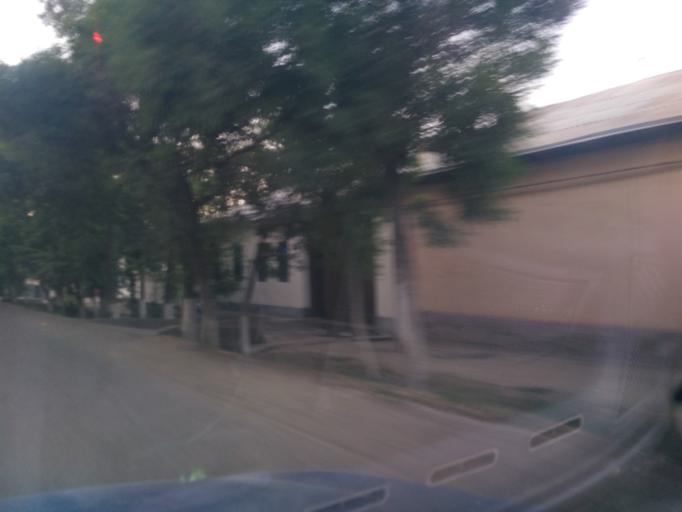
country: UZ
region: Sirdaryo
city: Guliston
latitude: 40.5024
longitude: 68.7692
